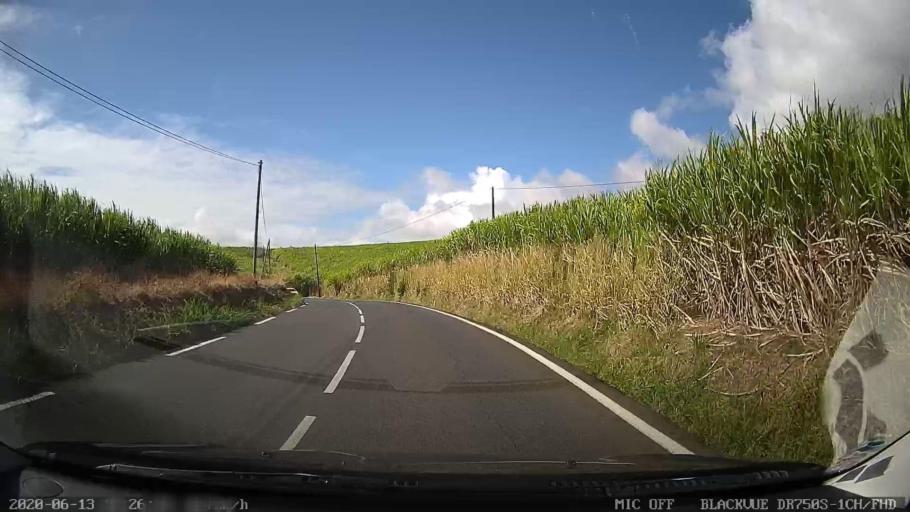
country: RE
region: Reunion
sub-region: Reunion
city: Sainte-Marie
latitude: -20.9205
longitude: 55.5403
